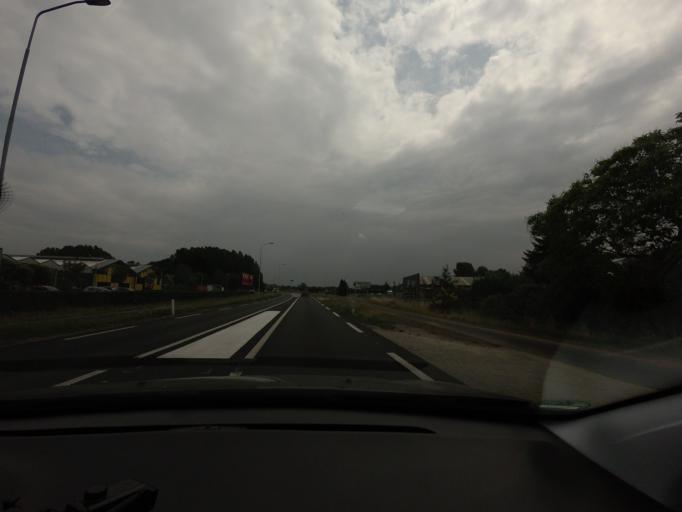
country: NL
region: Gelderland
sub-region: Gemeente Tiel
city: Tiel
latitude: 51.8890
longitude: 5.3876
